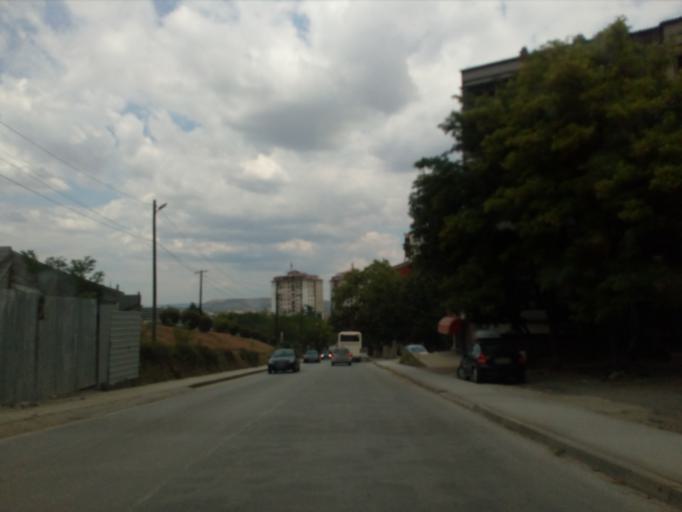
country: MK
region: Veles
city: Veles
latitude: 41.7110
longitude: 21.7638
